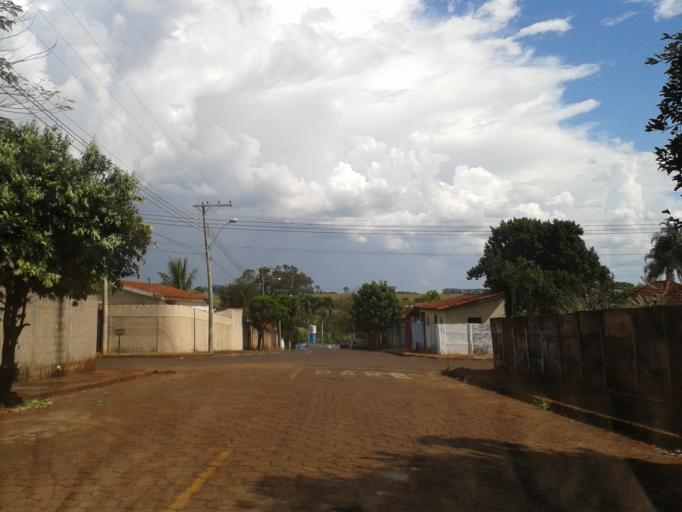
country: BR
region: Minas Gerais
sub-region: Centralina
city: Centralina
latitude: -18.7279
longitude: -49.2035
